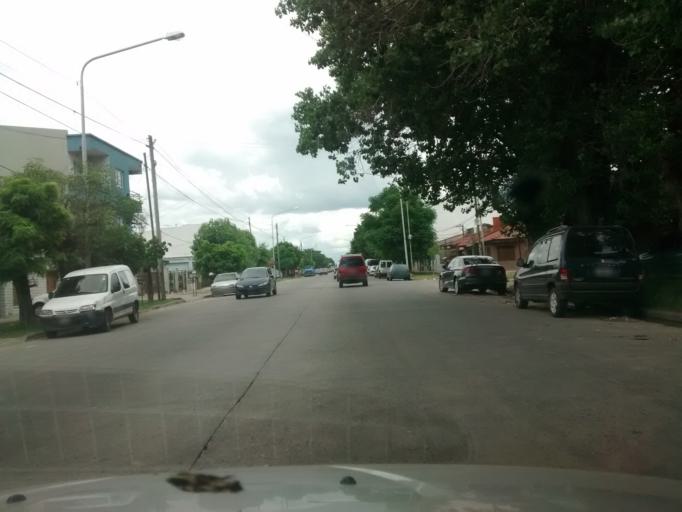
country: AR
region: Buenos Aires
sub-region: Partido de La Plata
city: La Plata
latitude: -34.9147
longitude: -57.9169
